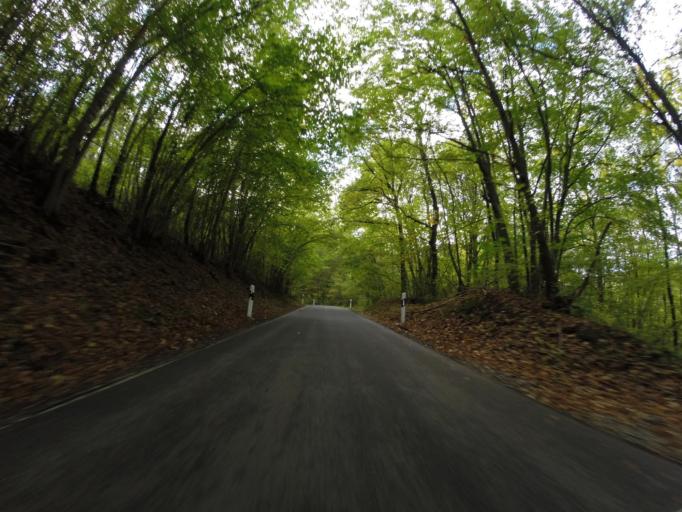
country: DE
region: Thuringia
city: Jena
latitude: 50.9390
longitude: 11.5432
